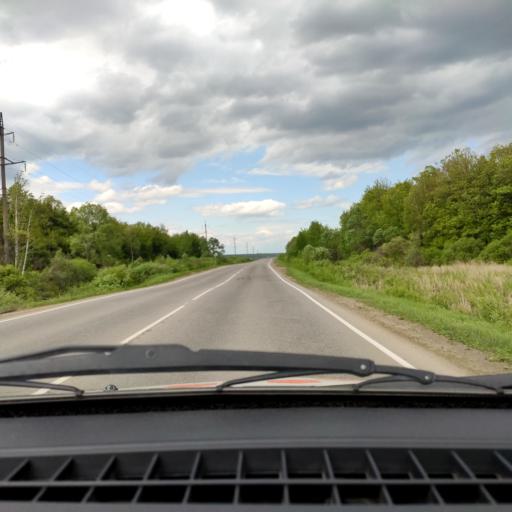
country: RU
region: Bashkortostan
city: Iglino
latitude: 54.8868
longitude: 56.4709
